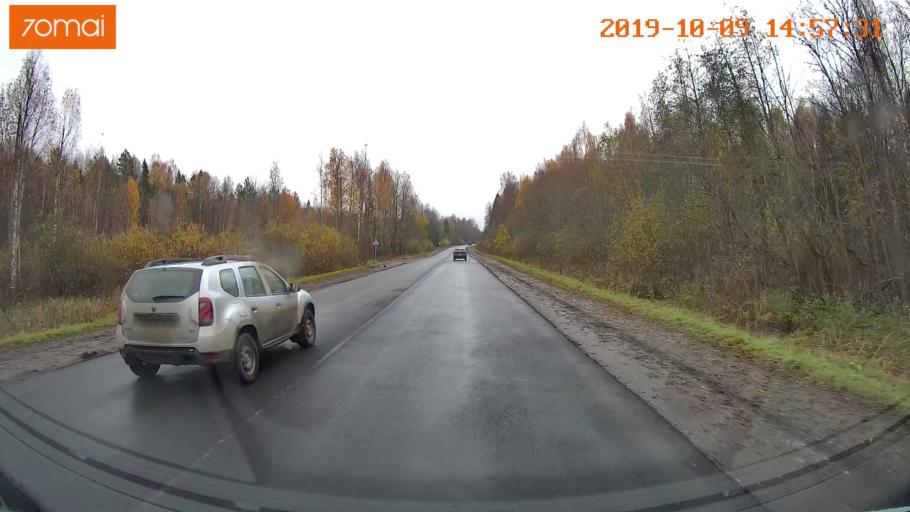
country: RU
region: Kostroma
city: Chistyye Bory
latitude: 58.3369
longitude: 41.6510
